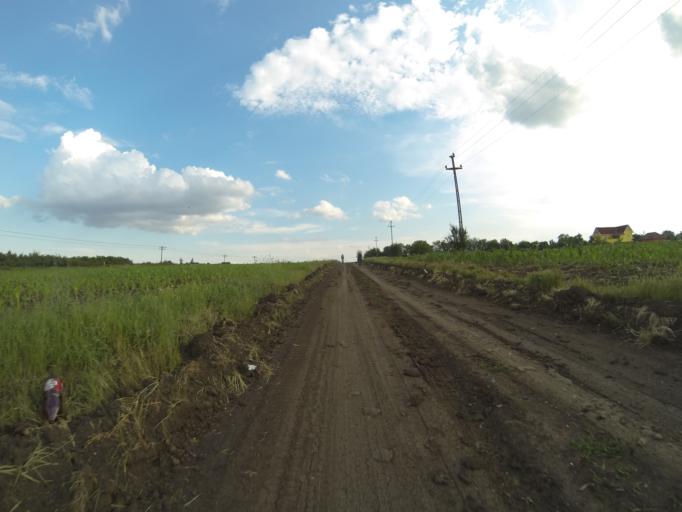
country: RO
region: Dolj
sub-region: Comuna Caloparu
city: Salcuta
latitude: 44.1576
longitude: 23.7061
